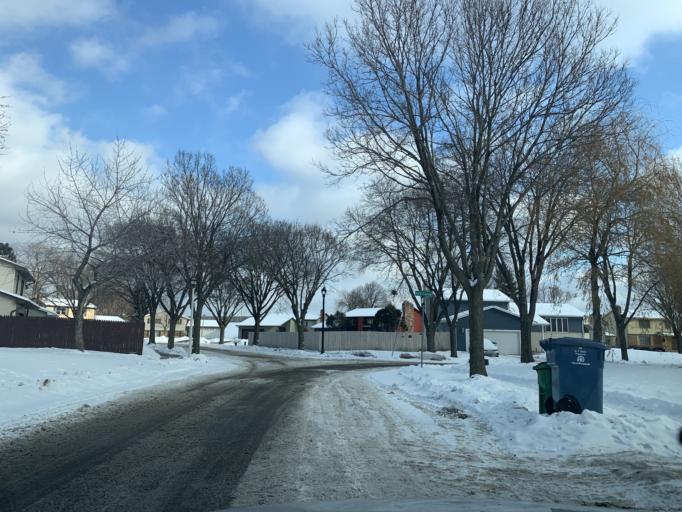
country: US
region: Minnesota
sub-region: Hennepin County
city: Minneapolis
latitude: 44.9947
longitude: -93.2865
